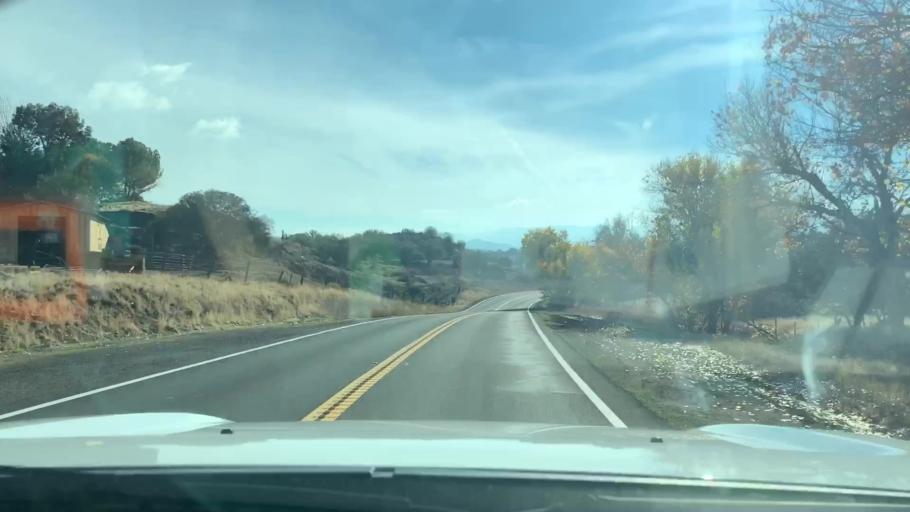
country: US
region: California
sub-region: Fresno County
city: Coalinga
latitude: 36.0856
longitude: -120.4891
